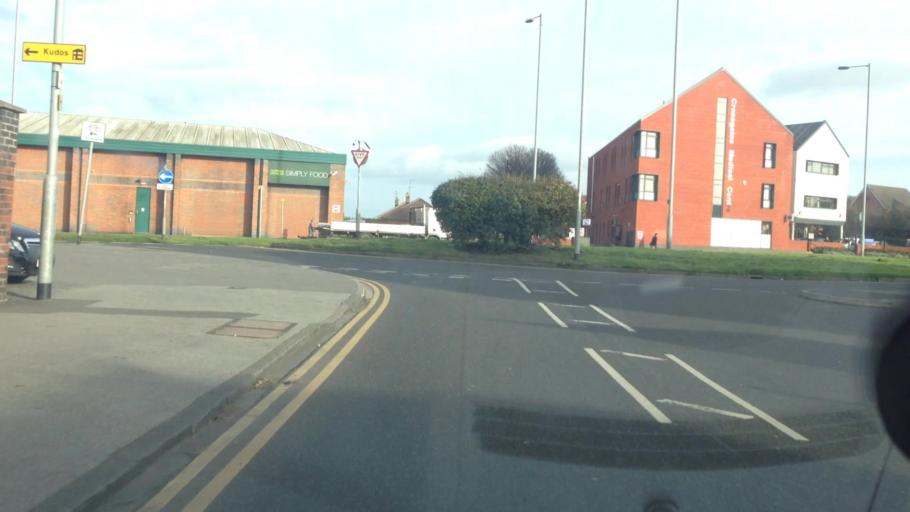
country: GB
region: England
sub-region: City and Borough of Leeds
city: Scholes
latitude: 53.8039
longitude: -1.4523
